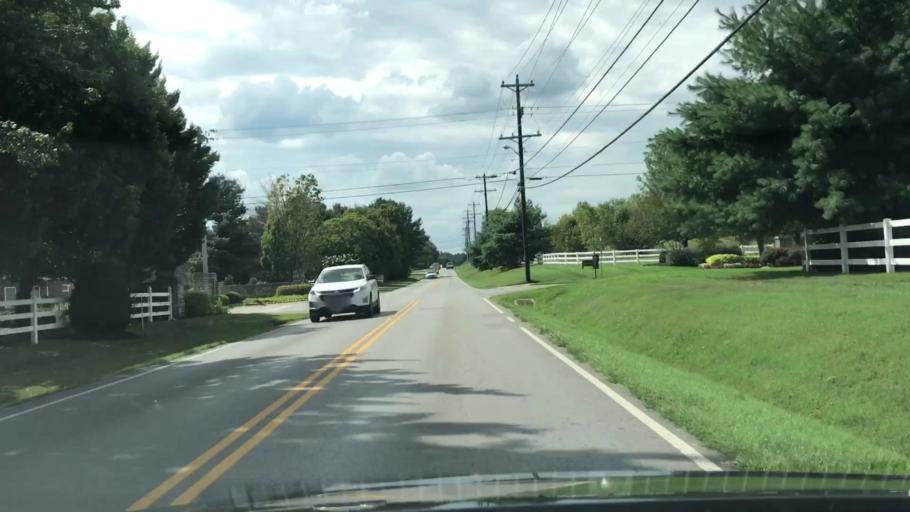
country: US
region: Tennessee
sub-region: Williamson County
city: Thompson's Station
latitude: 35.7823
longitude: -86.8984
